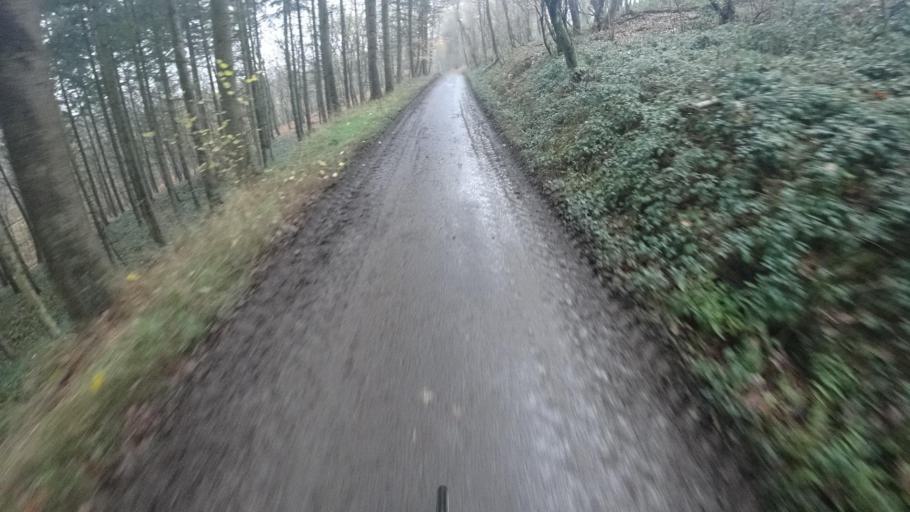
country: DE
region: Rheinland-Pfalz
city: Kesseling
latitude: 50.4970
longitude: 7.0155
